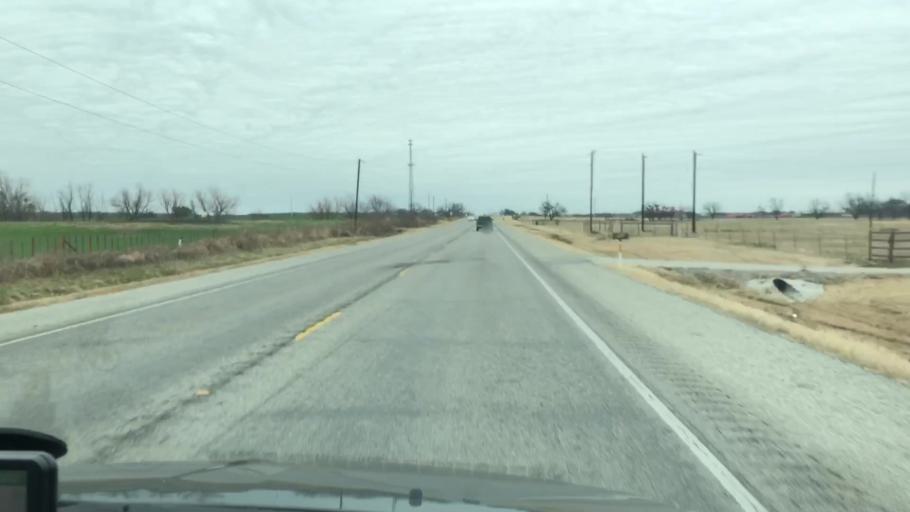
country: US
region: Texas
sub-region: Palo Pinto County
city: Mineral Wells
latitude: 32.9120
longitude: -98.0786
